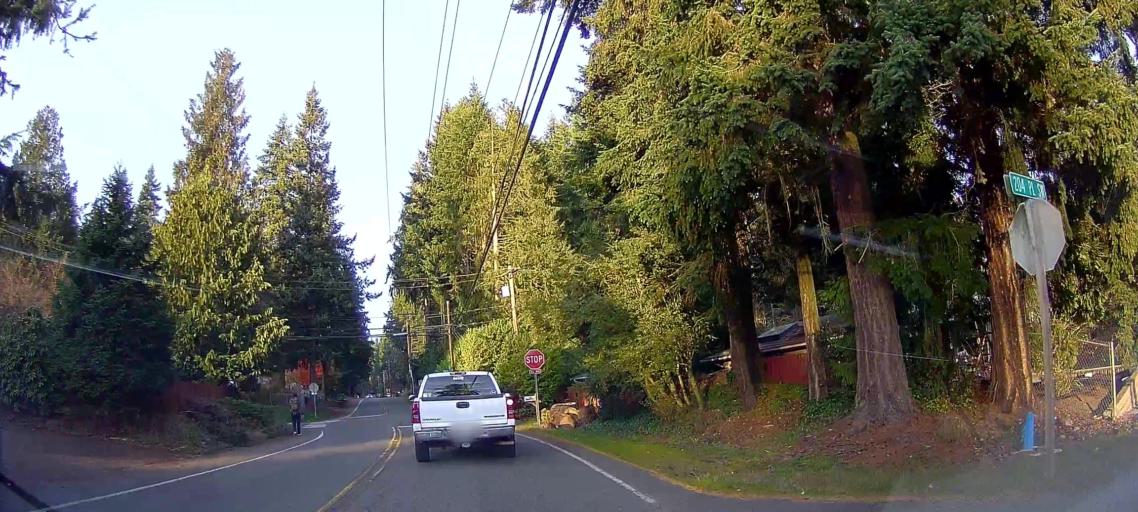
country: US
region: Washington
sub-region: Snohomish County
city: Alderwood Manor
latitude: 47.8131
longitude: -122.2584
